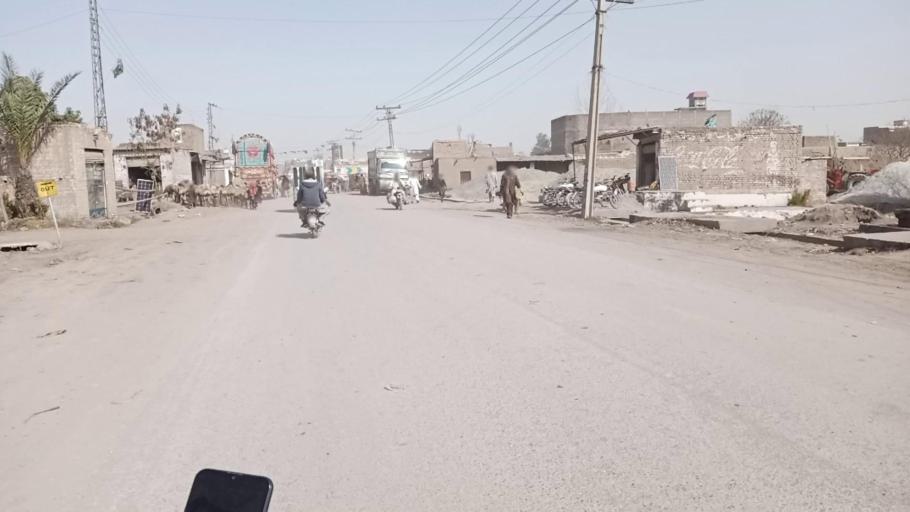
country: PK
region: Khyber Pakhtunkhwa
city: Peshawar
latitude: 33.9881
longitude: 71.6331
